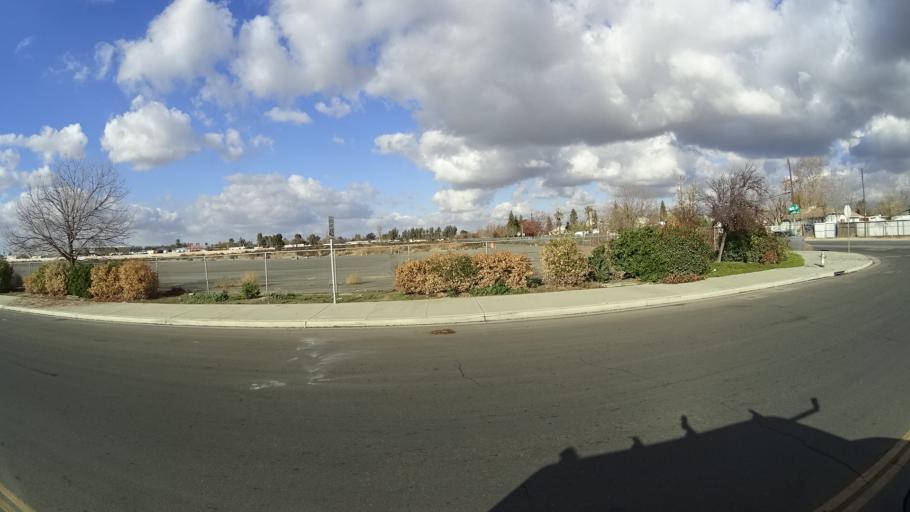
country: US
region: California
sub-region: Kern County
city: Bakersfield
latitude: 35.3322
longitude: -118.9948
